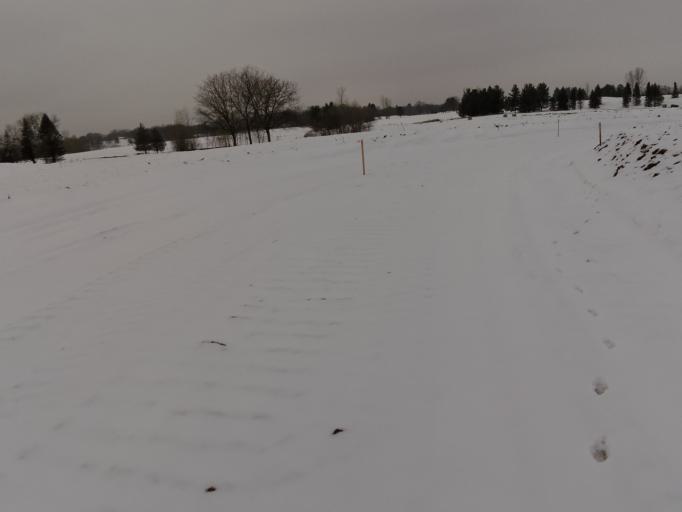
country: US
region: Minnesota
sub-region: Washington County
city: Lake Elmo
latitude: 44.9666
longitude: -92.8719
